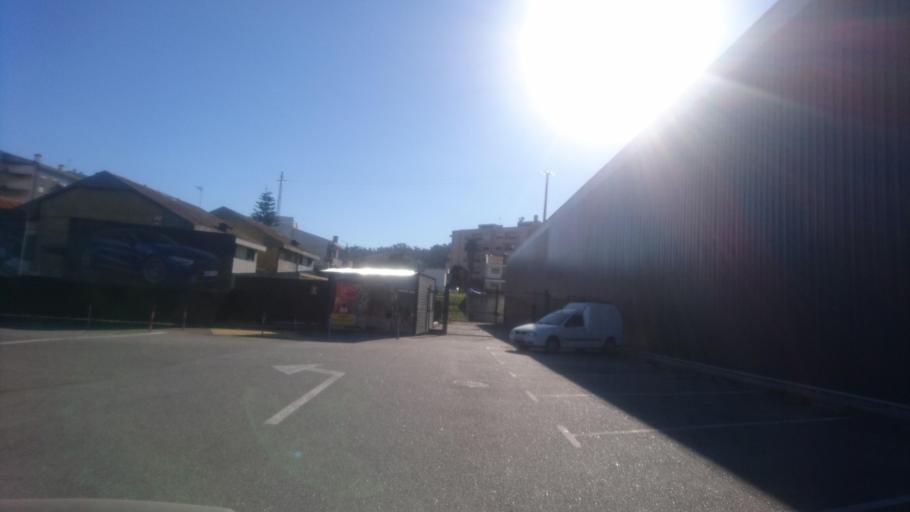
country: PT
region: Porto
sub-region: Valongo
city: Valongo
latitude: 41.1964
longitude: -8.5108
